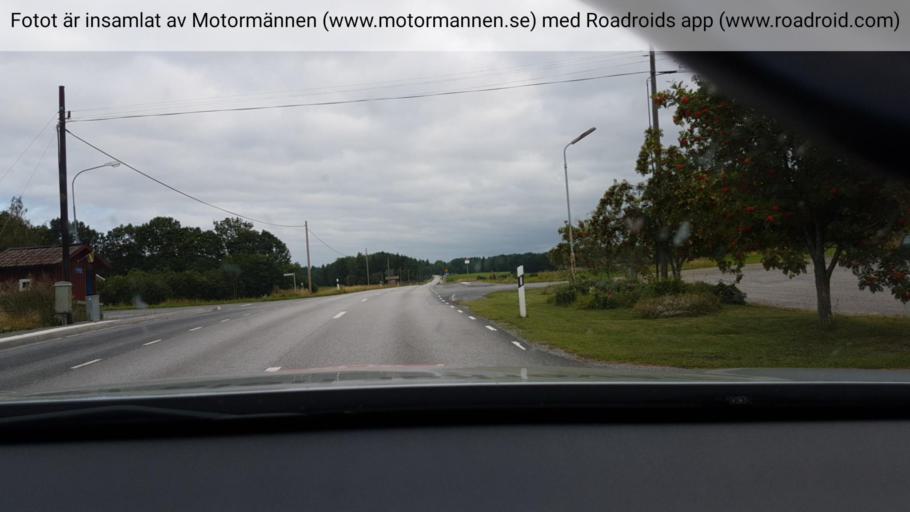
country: SE
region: Stockholm
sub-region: Norrtalje Kommun
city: Skanninge
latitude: 59.8409
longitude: 18.4418
